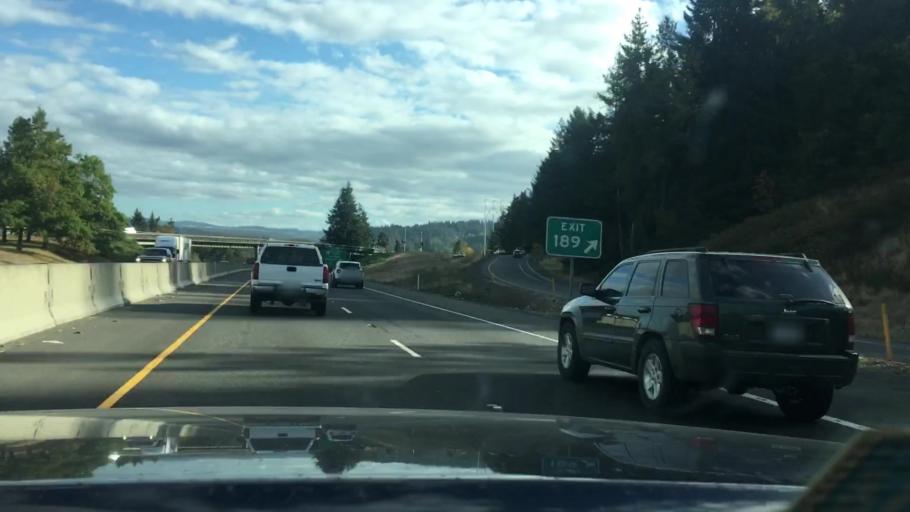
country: US
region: Oregon
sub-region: Lane County
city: Springfield
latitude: 44.0244
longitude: -123.0282
